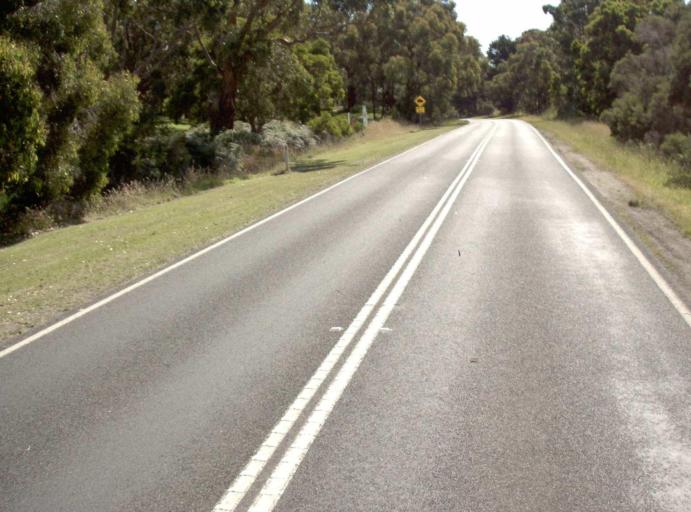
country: AU
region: Victoria
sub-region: Latrobe
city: Morwell
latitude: -38.6692
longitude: 146.3937
